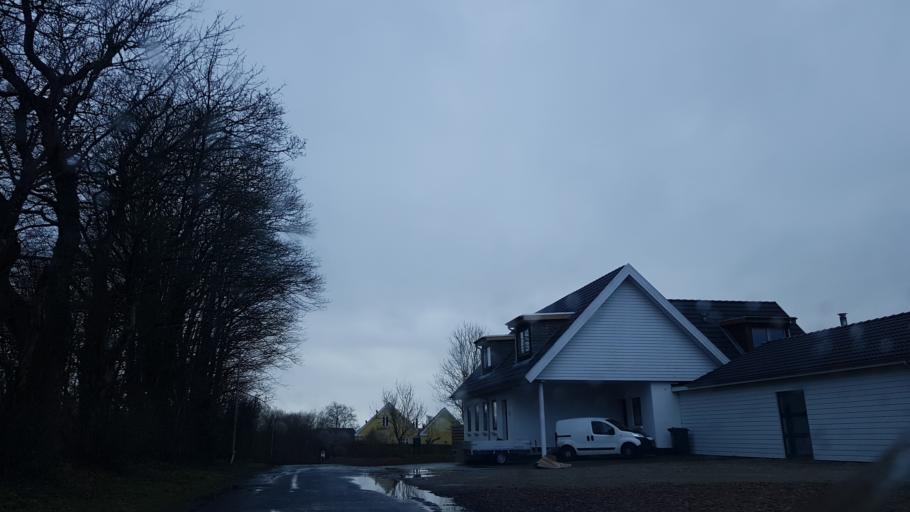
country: DK
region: South Denmark
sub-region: Kolding Kommune
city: Vamdrup
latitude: 55.3909
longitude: 9.3588
